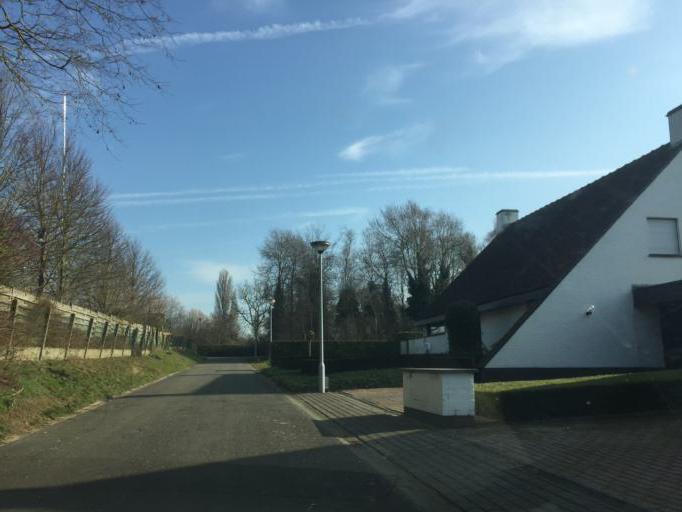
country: BE
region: Flanders
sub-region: Provincie West-Vlaanderen
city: Roeselare
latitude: 50.9276
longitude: 3.1207
